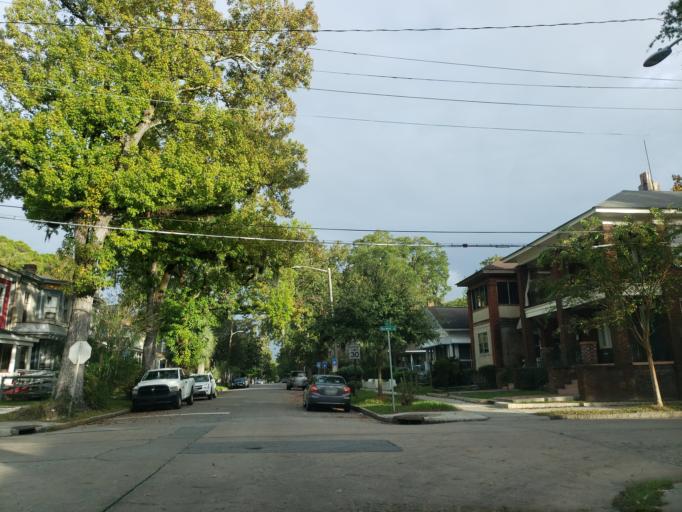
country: US
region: Georgia
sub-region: Chatham County
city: Savannah
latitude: 32.0612
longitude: -81.0834
